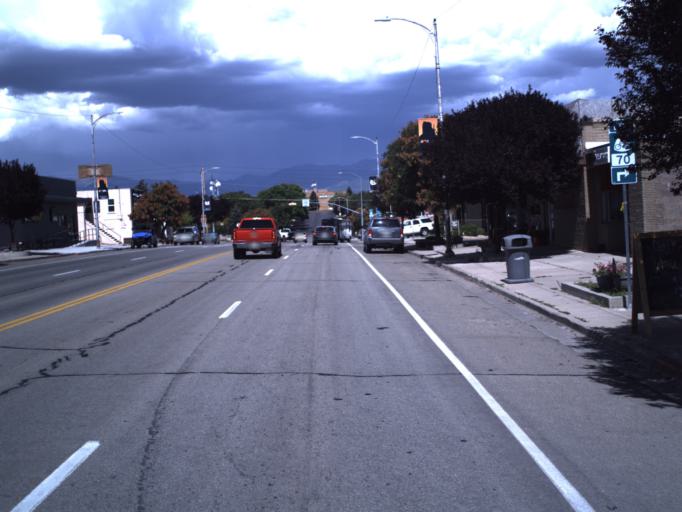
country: US
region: Utah
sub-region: San Juan County
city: Blanding
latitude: 37.6241
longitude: -109.4780
